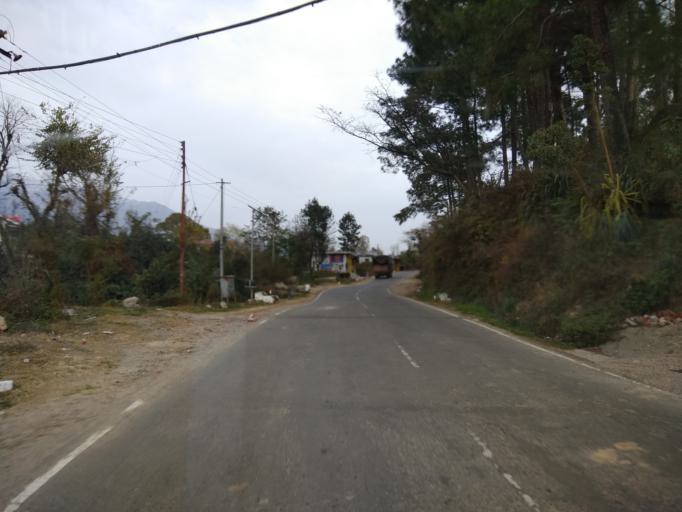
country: IN
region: Himachal Pradesh
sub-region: Kangra
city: Palampur
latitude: 32.1150
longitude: 76.5141
